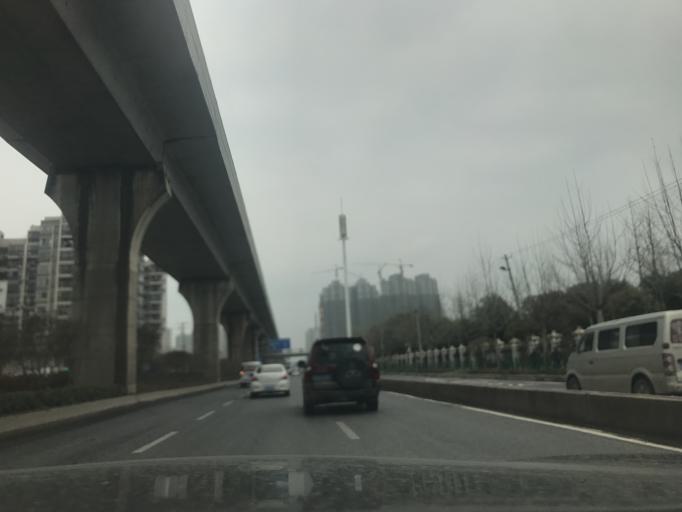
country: CN
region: Hubei
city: Houhu
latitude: 30.6622
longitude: 114.3306
